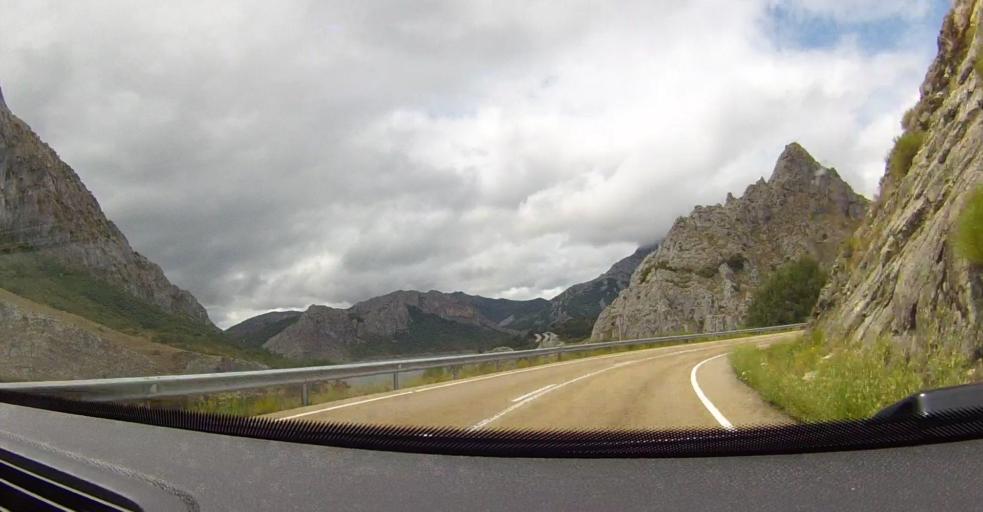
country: ES
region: Castille and Leon
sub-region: Provincia de Leon
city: Reyero
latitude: 42.9580
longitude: -5.2511
